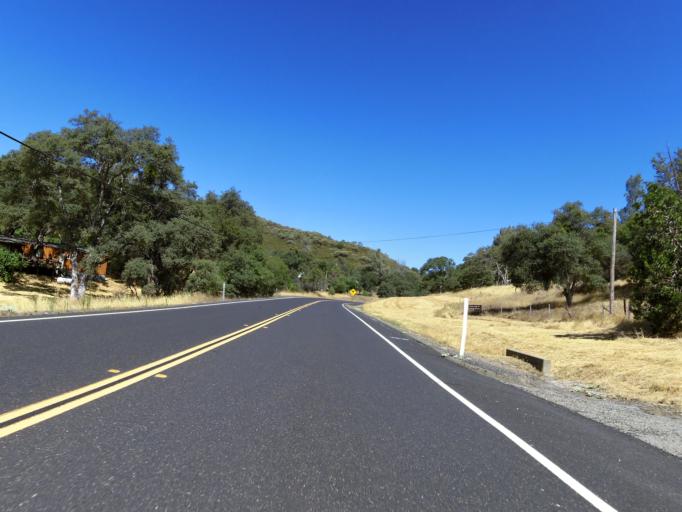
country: US
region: California
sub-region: Tuolumne County
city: Tuolumne City
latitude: 37.7077
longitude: -120.2012
